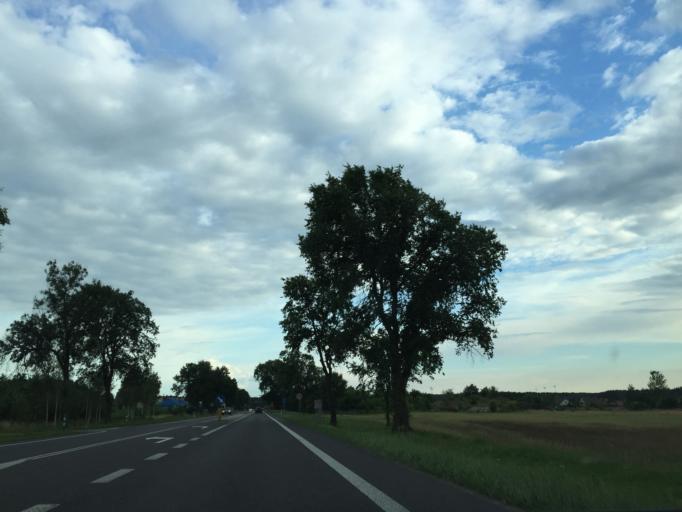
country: PL
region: Lublin Voivodeship
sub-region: Powiat lubartowski
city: Firlej
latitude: 51.5639
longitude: 22.5031
